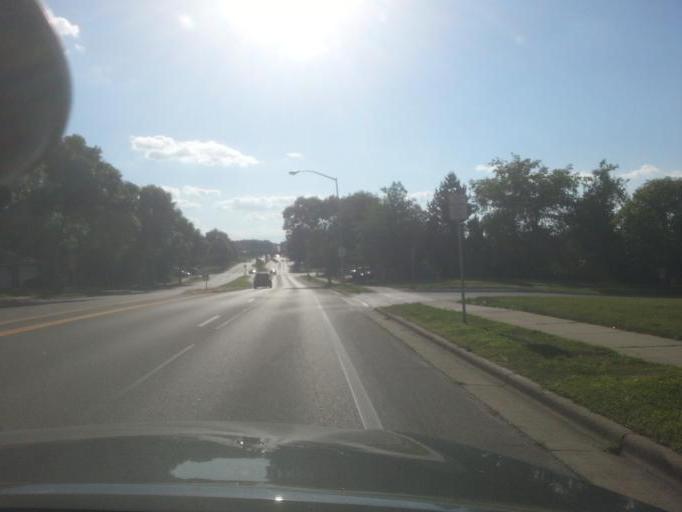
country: US
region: Wisconsin
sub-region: Dane County
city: Middleton
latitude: 43.0752
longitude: -89.5167
